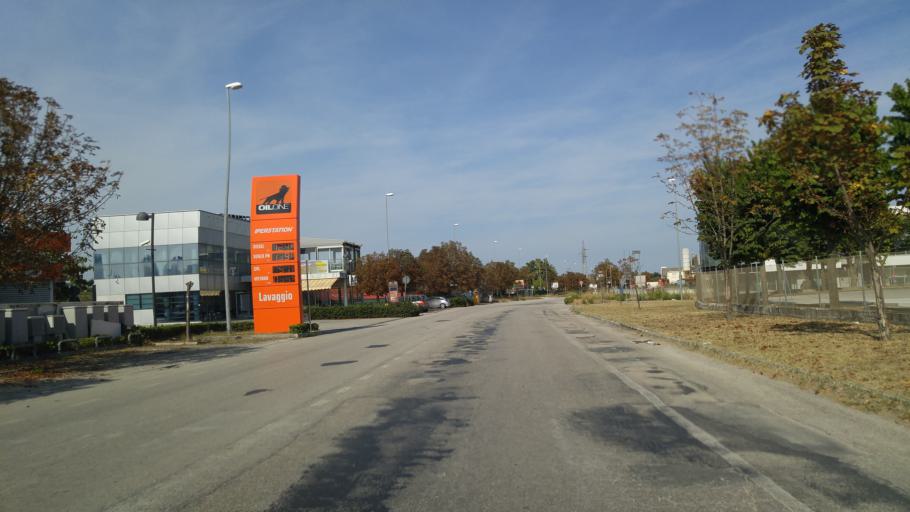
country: IT
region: The Marches
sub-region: Provincia di Pesaro e Urbino
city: Bellocchi
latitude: 43.7941
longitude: 13.0042
